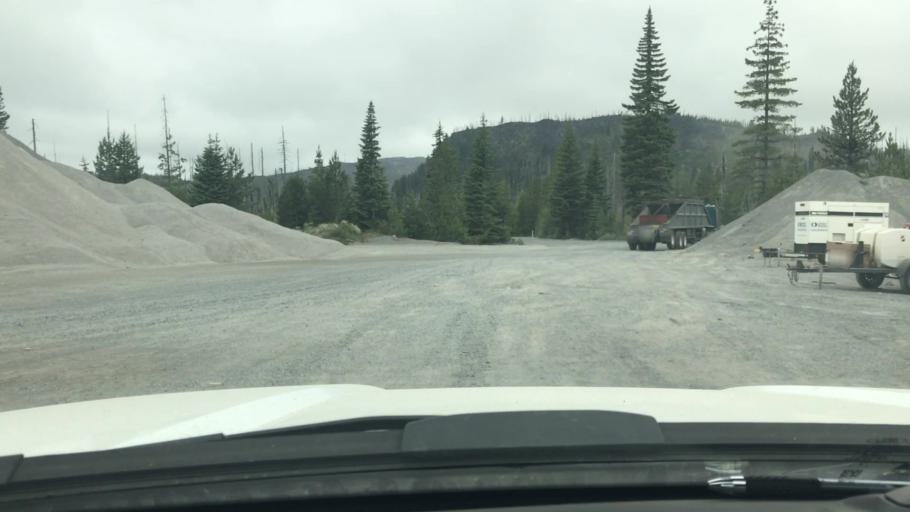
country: US
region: Oregon
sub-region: Deschutes County
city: Sisters
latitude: 44.4196
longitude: -121.8575
